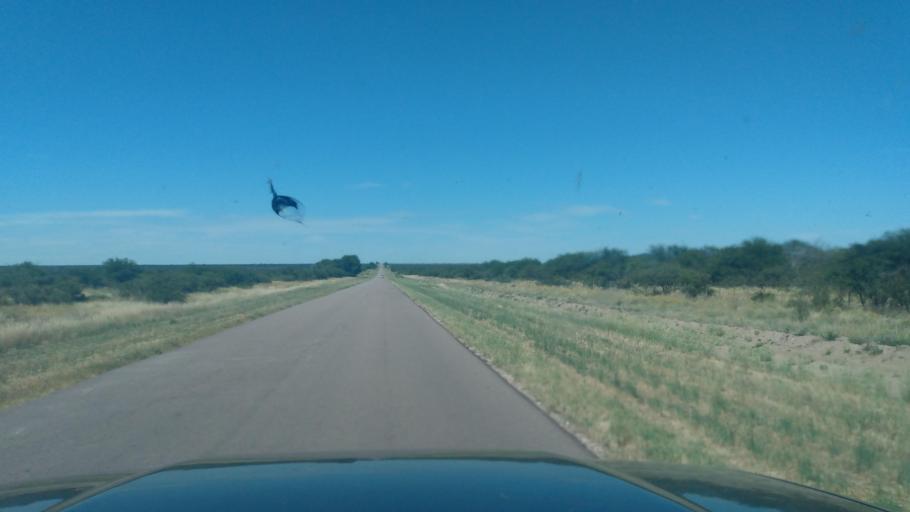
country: AR
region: La Pampa
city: General Acha
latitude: -37.5312
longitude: -65.1533
